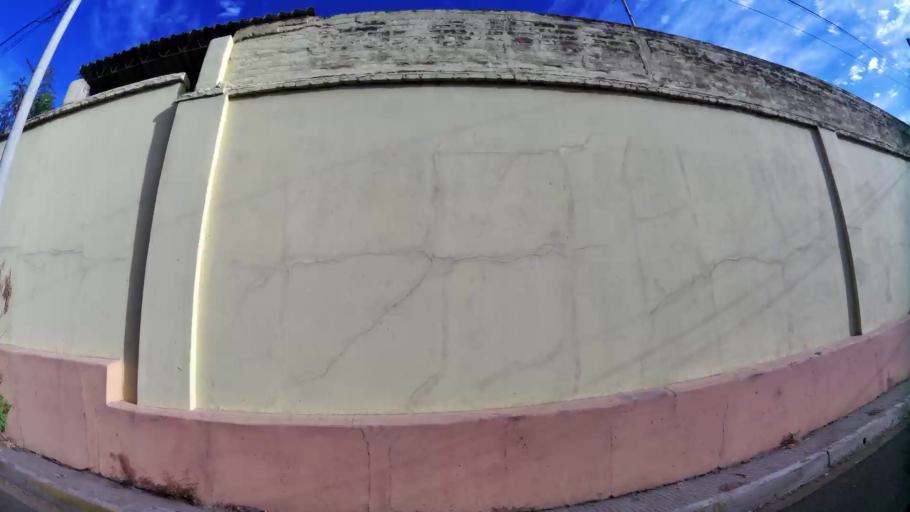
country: SV
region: Santa Ana
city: Santa Ana
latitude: 13.9976
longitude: -89.5621
